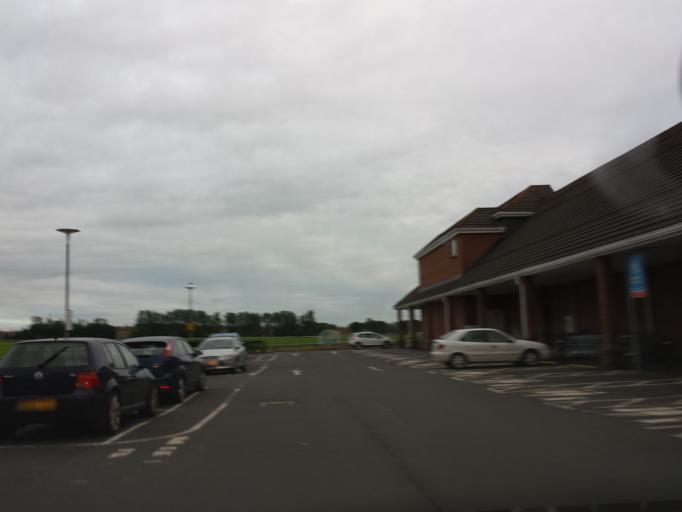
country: GB
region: Scotland
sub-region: South Ayrshire
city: Prestwick
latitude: 55.4679
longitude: -4.6070
